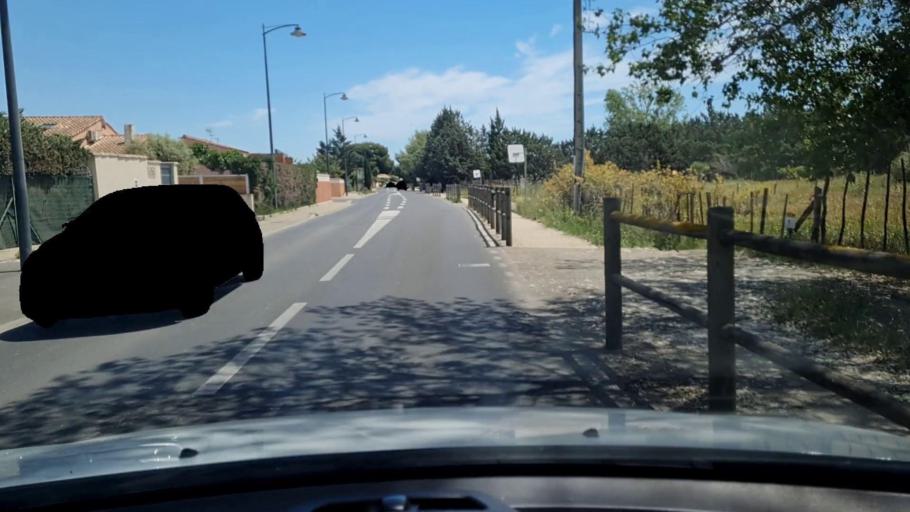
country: FR
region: Languedoc-Roussillon
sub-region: Departement du Gard
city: Aigues-Mortes
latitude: 43.5716
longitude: 4.1780
